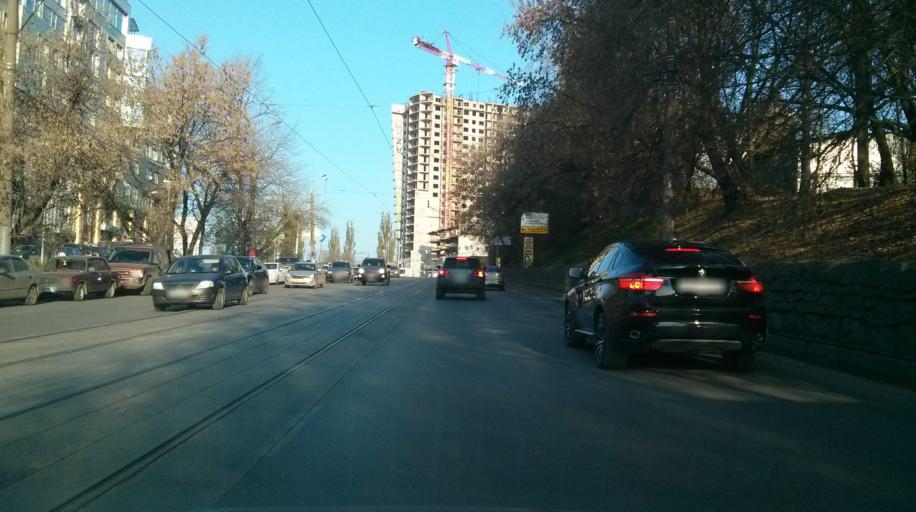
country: RU
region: Nizjnij Novgorod
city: Nizhniy Novgorod
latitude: 56.3213
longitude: 44.0324
